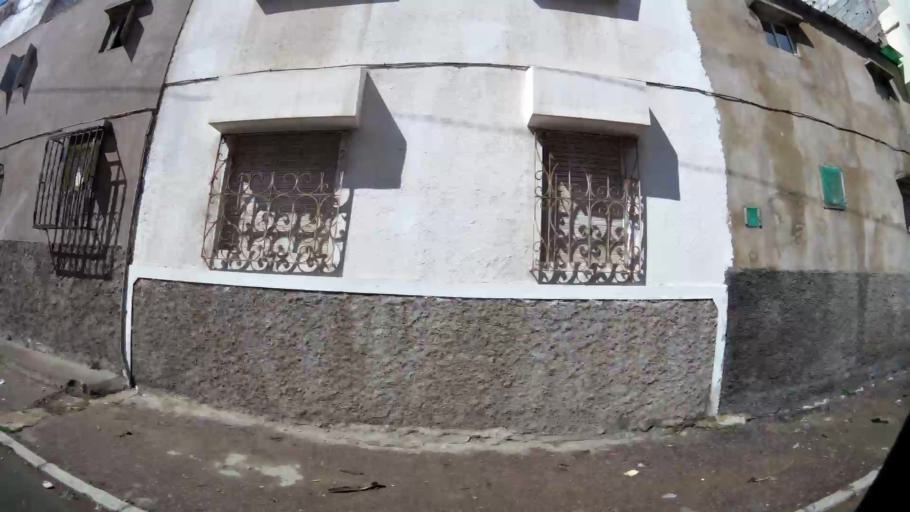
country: MA
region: Grand Casablanca
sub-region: Casablanca
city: Casablanca
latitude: 33.5700
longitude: -7.6842
